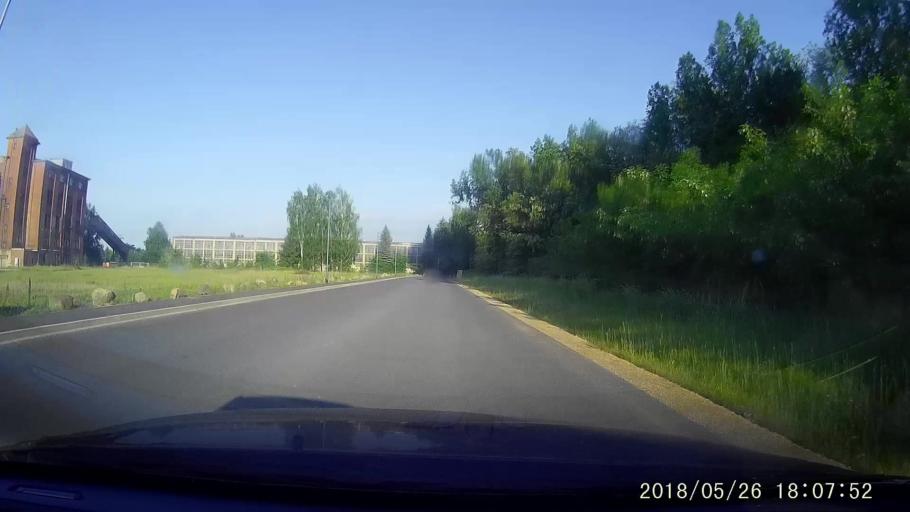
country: DE
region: Saxony
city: Schonau-Berzdorf
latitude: 51.0686
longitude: 14.9303
